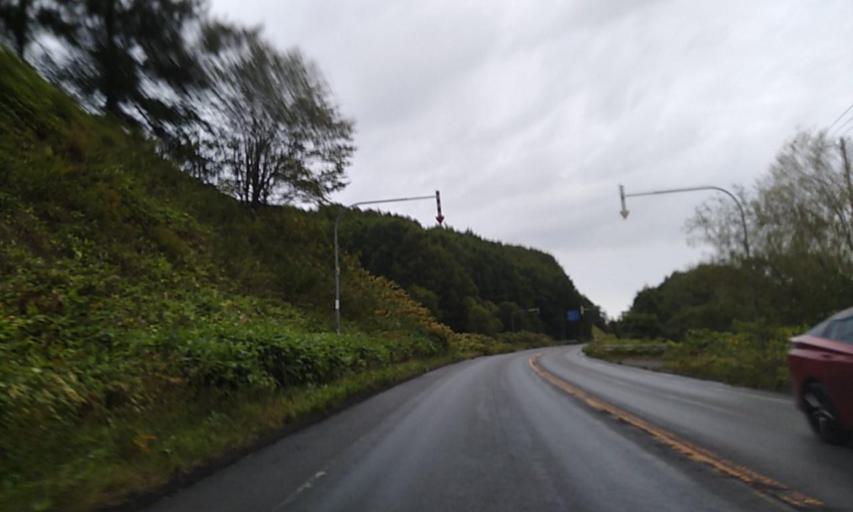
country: JP
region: Hokkaido
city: Mombetsu
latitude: 44.4880
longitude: 143.0791
